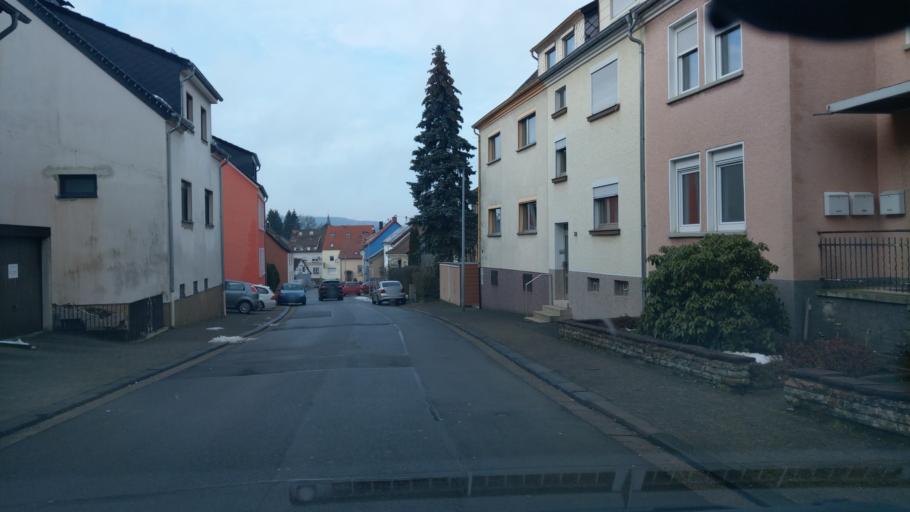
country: DE
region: Saarland
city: Hangard
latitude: 49.3680
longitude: 7.1917
